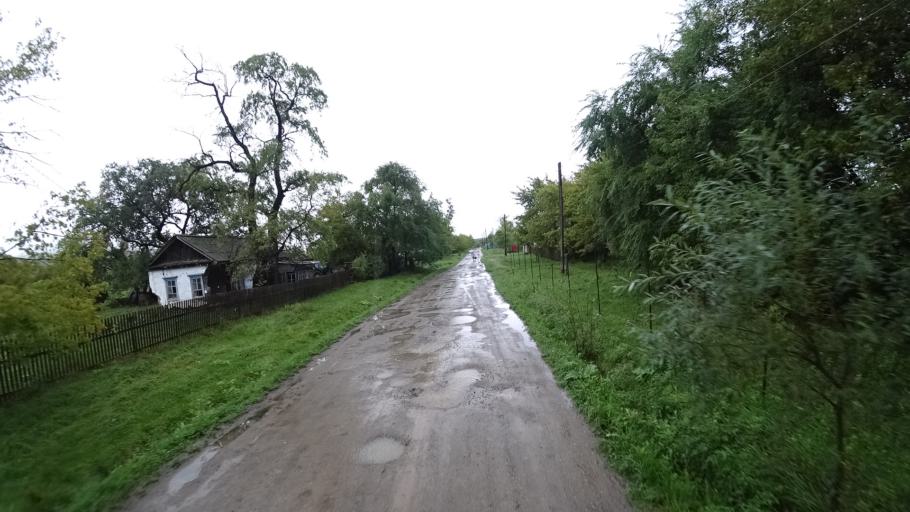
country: RU
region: Primorskiy
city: Monastyrishche
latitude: 44.2539
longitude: 132.4267
